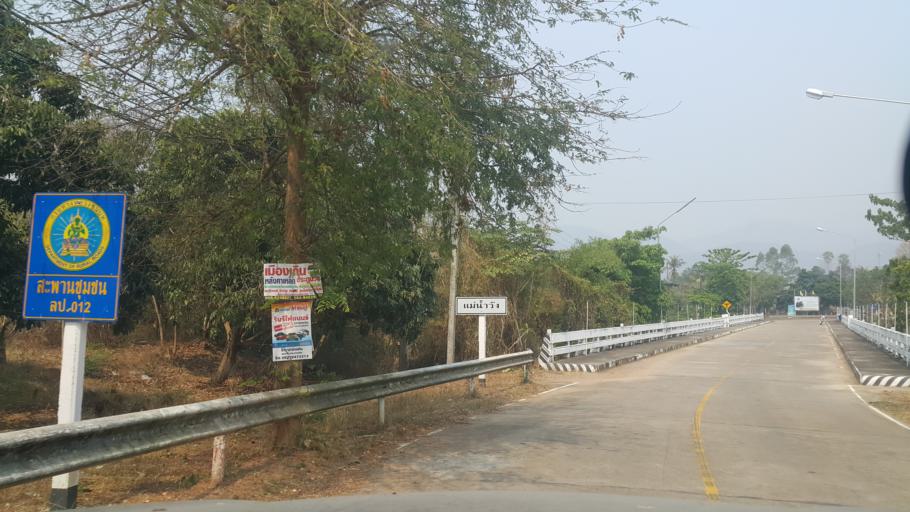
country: TH
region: Lampang
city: Thoen
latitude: 17.7513
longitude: 99.2312
